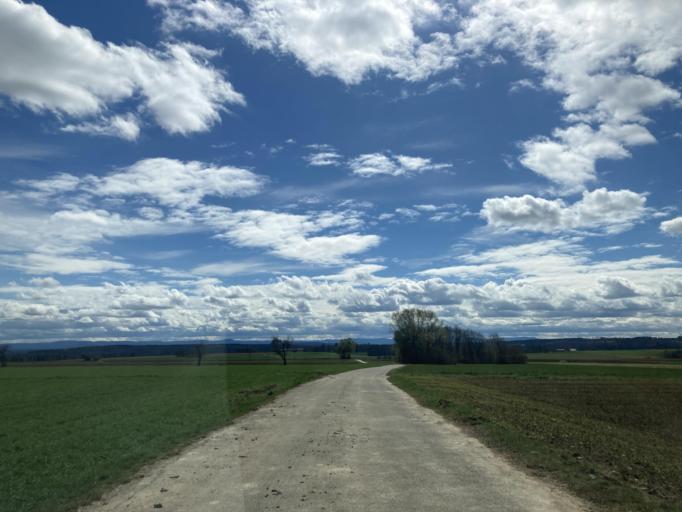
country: DE
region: Baden-Wuerttemberg
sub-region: Regierungsbezirk Stuttgart
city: Bondorf
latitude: 48.4686
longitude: 8.8155
